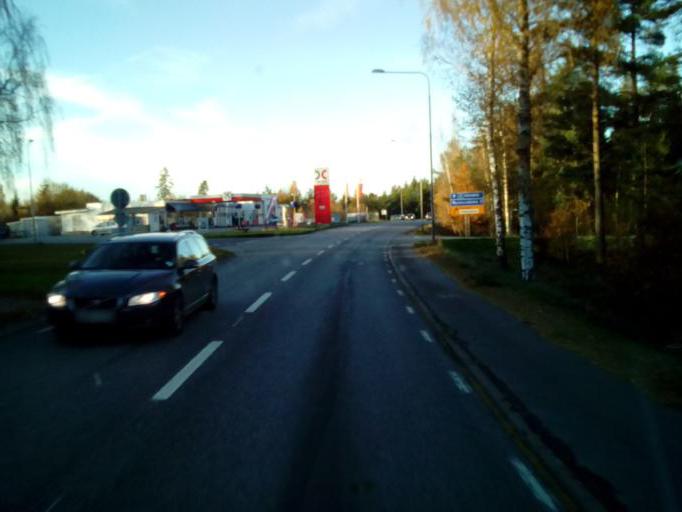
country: SE
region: OErebro
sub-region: Hallsbergs Kommun
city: Palsboda
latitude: 59.0714
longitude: 15.3326
